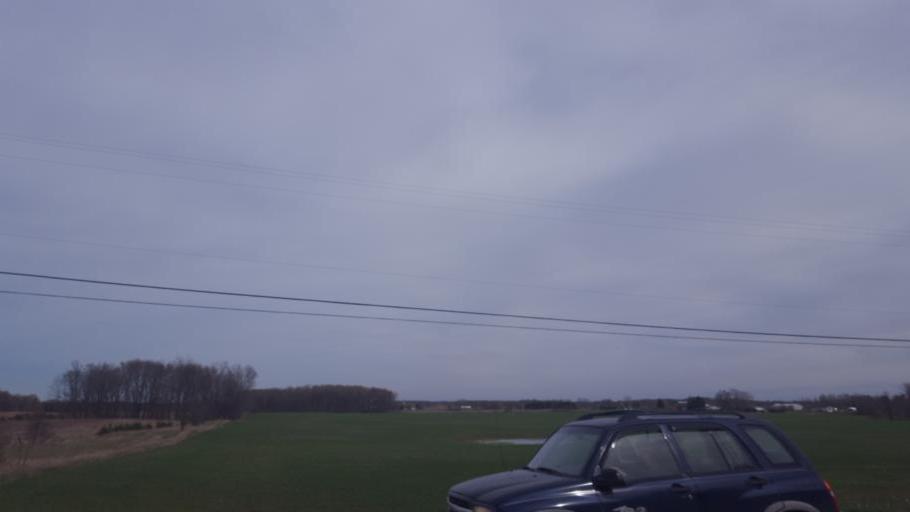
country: US
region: Michigan
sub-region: Clare County
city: Clare
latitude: 43.8618
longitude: -84.7681
